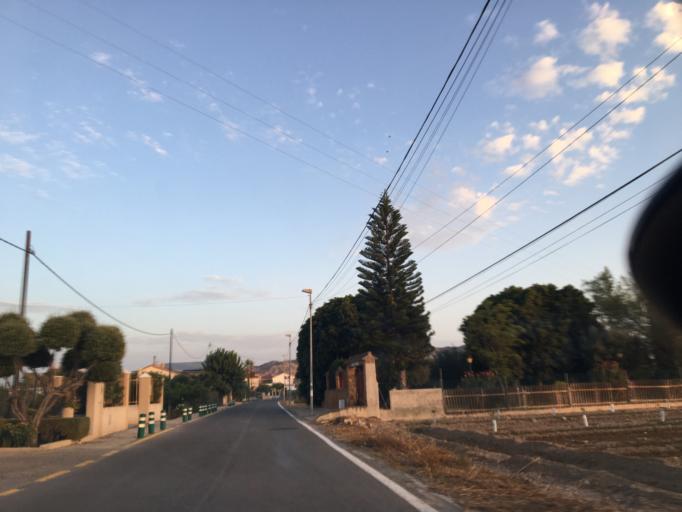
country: ES
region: Murcia
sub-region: Murcia
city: Santomera
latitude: 38.0235
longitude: -1.0548
